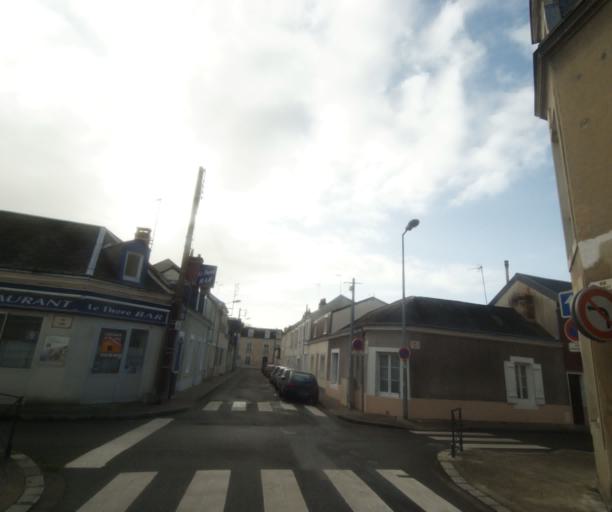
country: FR
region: Pays de la Loire
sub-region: Departement de la Sarthe
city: Le Mans
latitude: 47.9989
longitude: 0.2068
